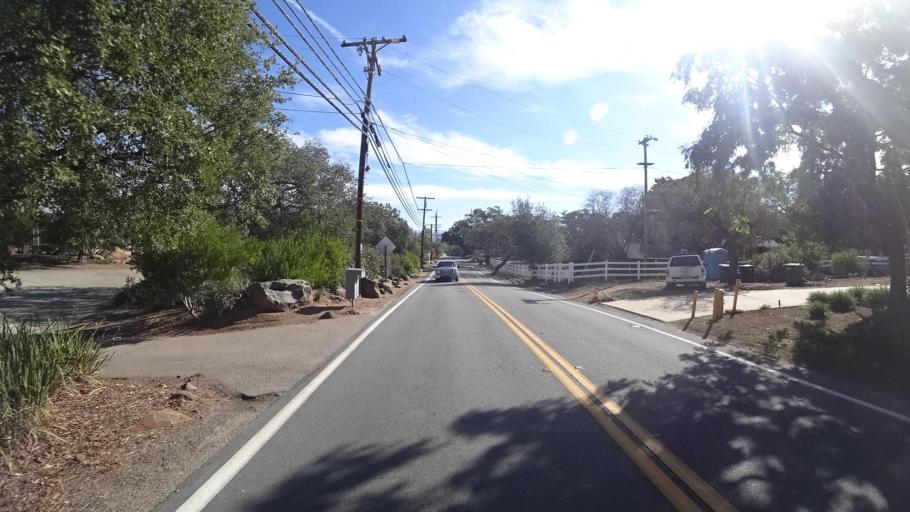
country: US
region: California
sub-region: San Diego County
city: Alpine
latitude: 32.8190
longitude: -116.7909
